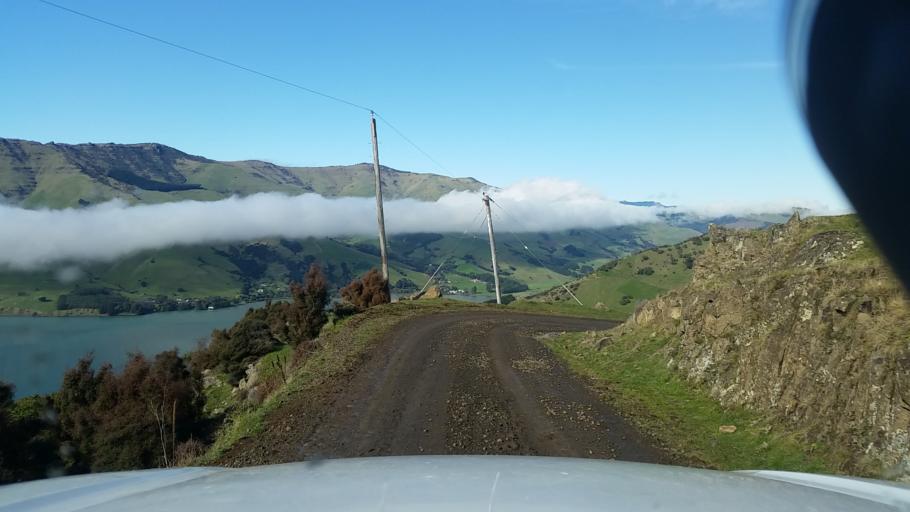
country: NZ
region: Canterbury
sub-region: Christchurch City
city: Christchurch
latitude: -43.6670
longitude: 172.8763
